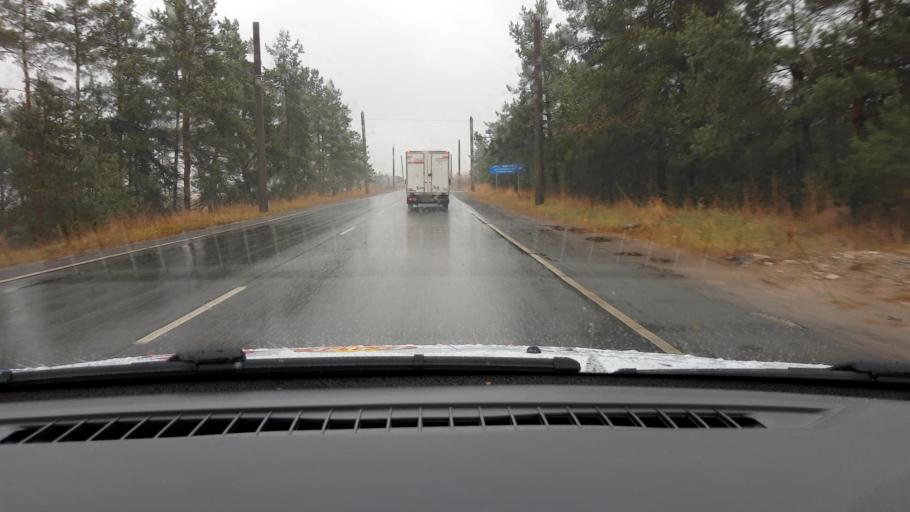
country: RU
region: Nizjnij Novgorod
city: Babino
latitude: 56.2765
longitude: 43.5591
